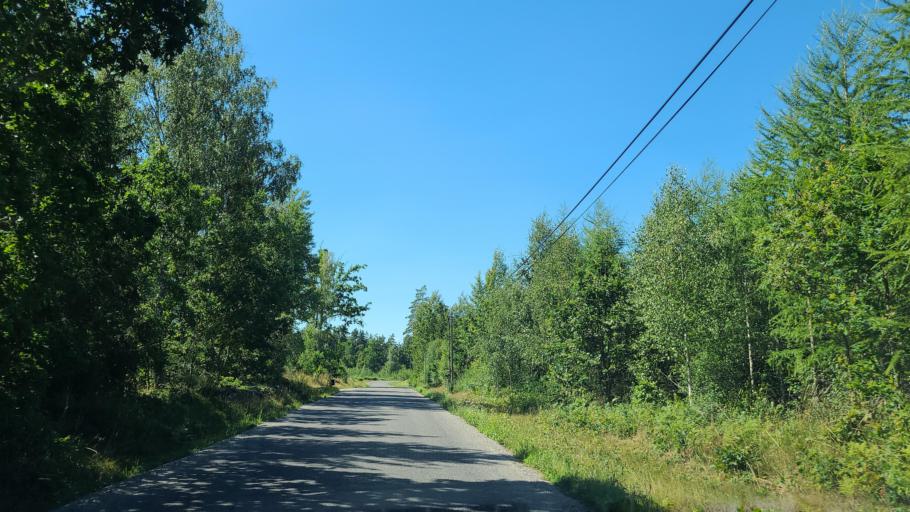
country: SE
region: Kalmar
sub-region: Kalmar Kommun
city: Ljungbyholm
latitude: 56.5718
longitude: 16.0728
